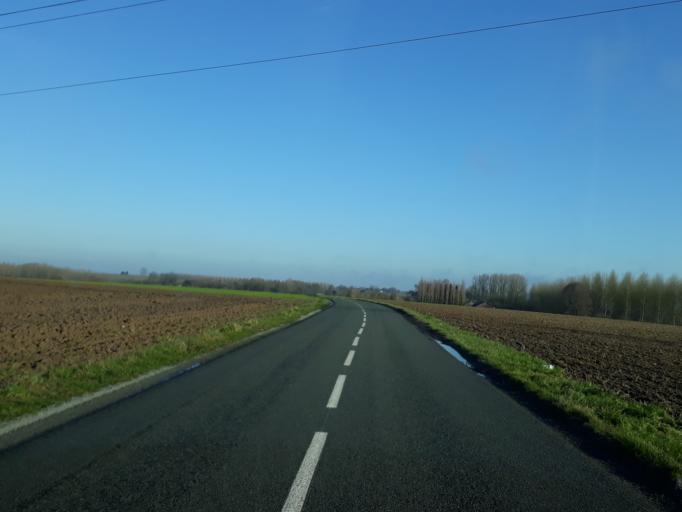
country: FR
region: Nord-Pas-de-Calais
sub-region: Departement du Nord
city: Wargnies-le-Grand
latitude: 50.3102
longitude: 3.6707
